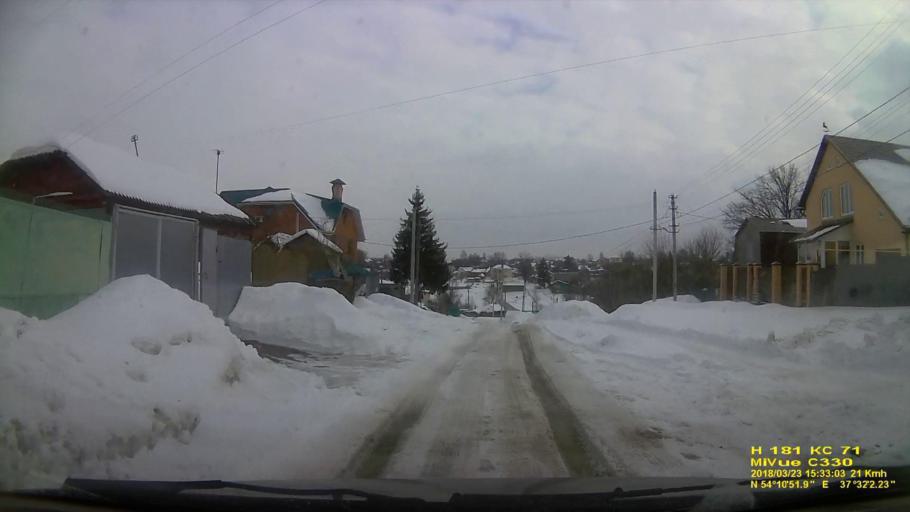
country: RU
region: Tula
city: Kosaya Gora
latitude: 54.1810
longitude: 37.5340
